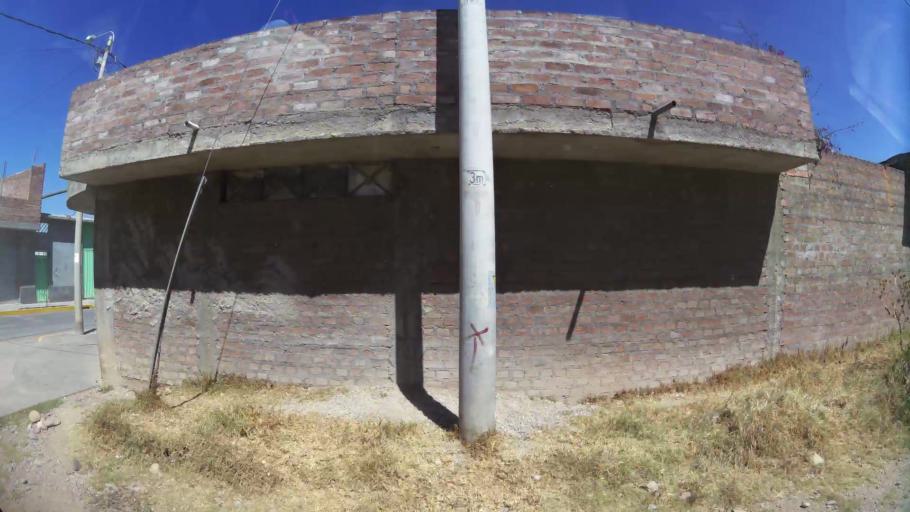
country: PE
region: Junin
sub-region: Provincia de Concepcion
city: Concepcion
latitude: -11.9164
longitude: -75.3200
